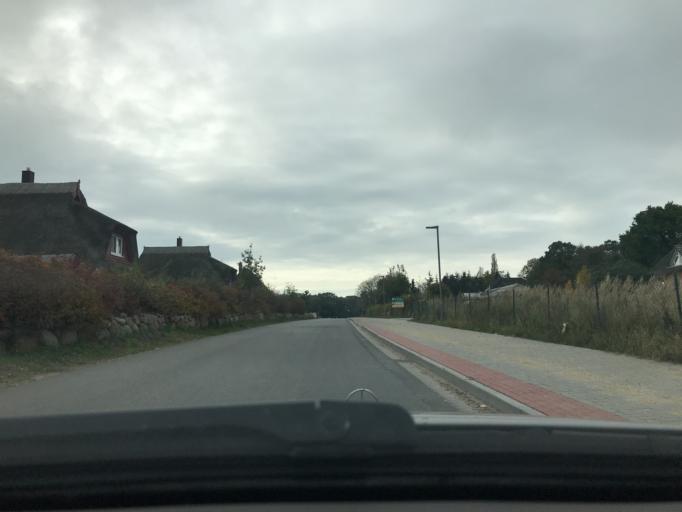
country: DE
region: Mecklenburg-Vorpommern
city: Ostseebad Zinnowitz
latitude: 54.0633
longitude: 13.9055
